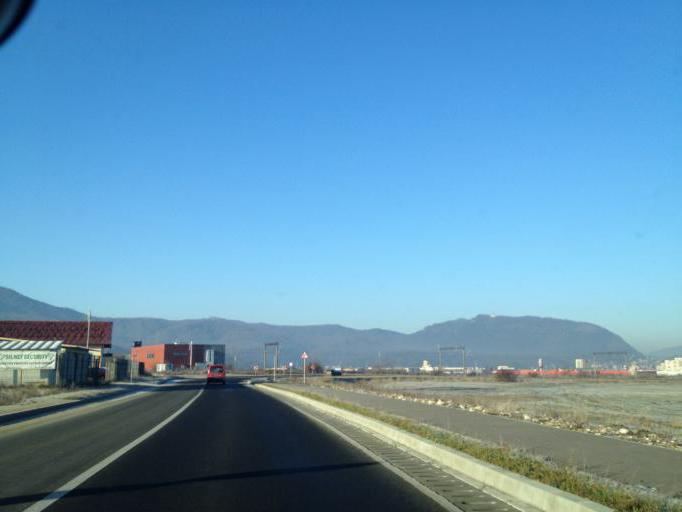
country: RO
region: Brasov
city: Brasov
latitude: 45.6286
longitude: 25.6504
